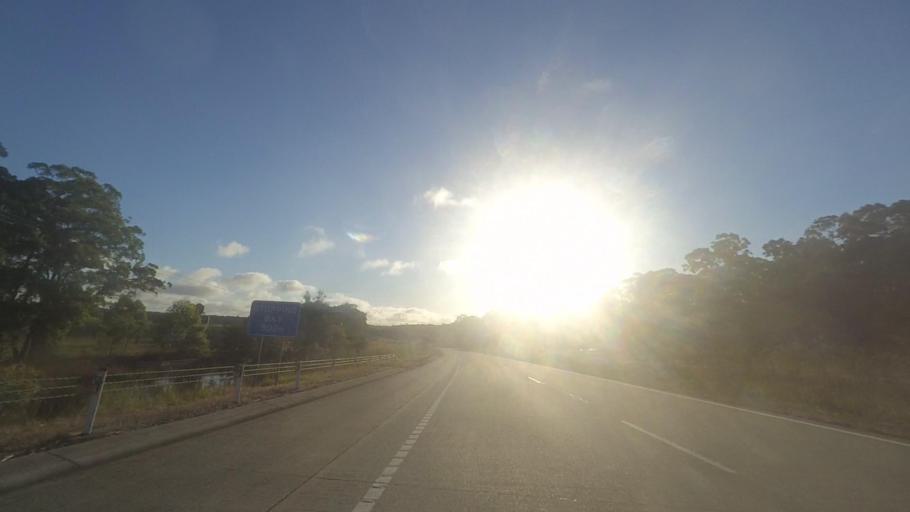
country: AU
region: New South Wales
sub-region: Great Lakes
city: Hawks Nest
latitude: -32.5377
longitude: 152.1719
